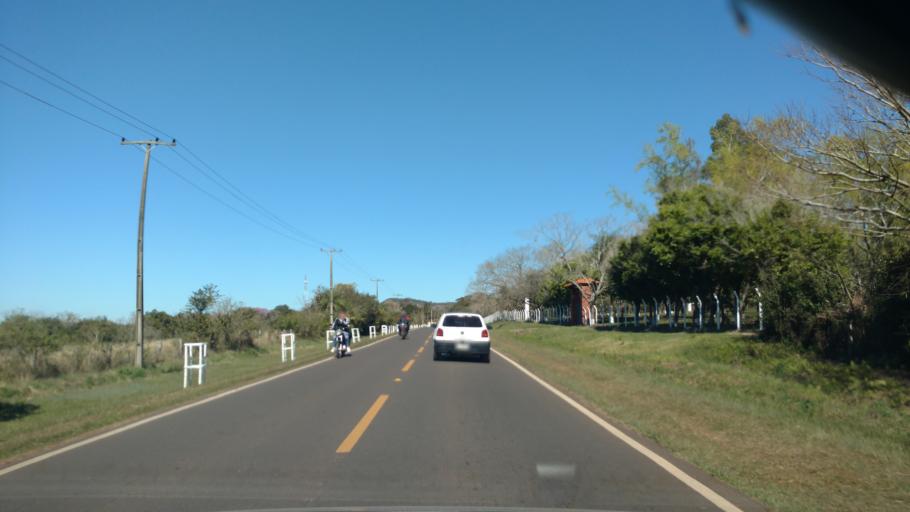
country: PY
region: Paraguari
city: Yaguaron
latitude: -25.5486
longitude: -57.2808
